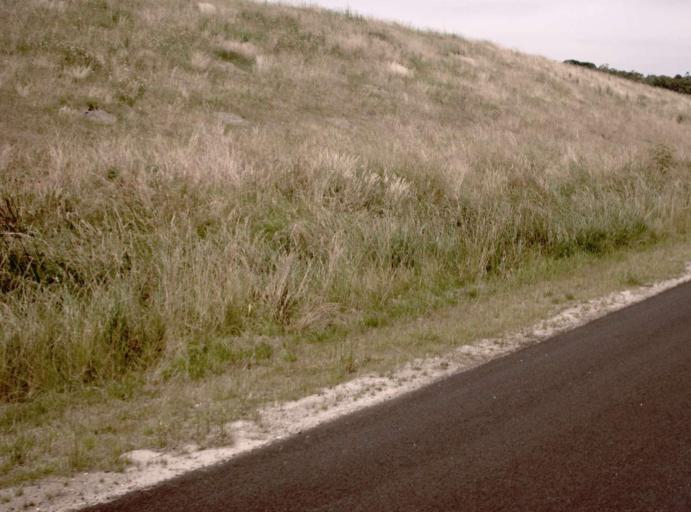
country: AU
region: Victoria
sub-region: Mornington Peninsula
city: Moorooduc
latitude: -38.2648
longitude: 145.1044
